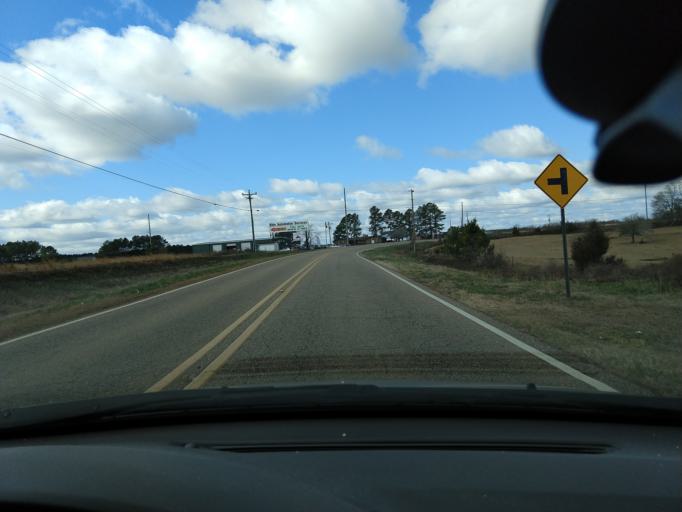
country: US
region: Alabama
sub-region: Coffee County
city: Enterprise
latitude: 31.3127
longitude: -85.9278
